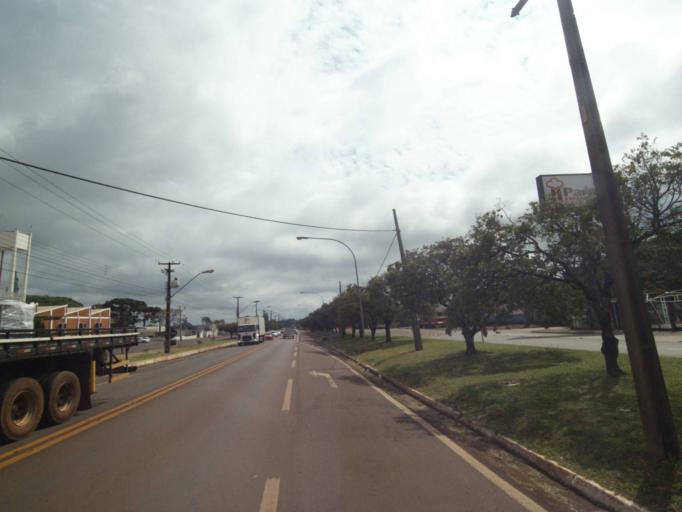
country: BR
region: Parana
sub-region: Campo Mourao
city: Campo Mourao
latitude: -24.0270
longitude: -52.3650
